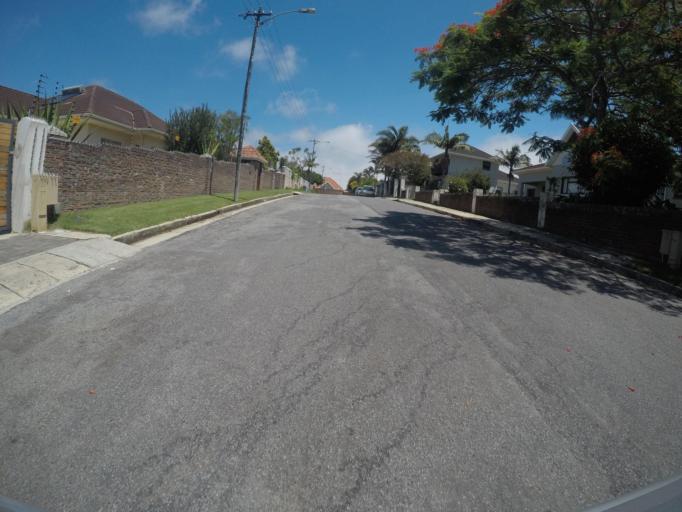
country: ZA
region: Eastern Cape
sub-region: Buffalo City Metropolitan Municipality
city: East London
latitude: -32.9869
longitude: 27.9074
